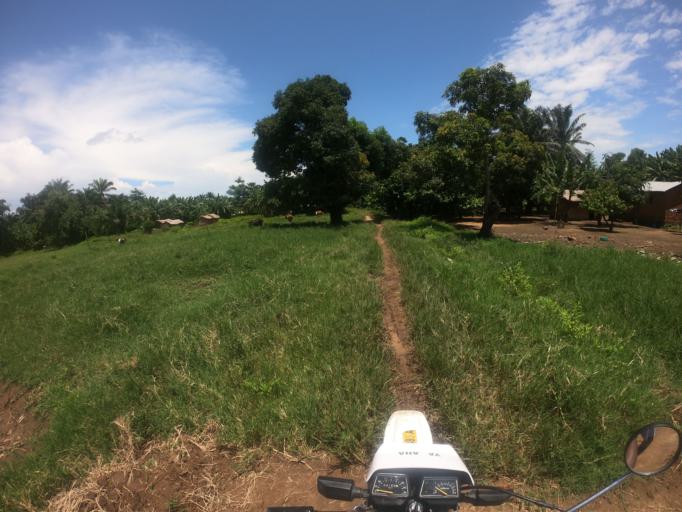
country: TZ
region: Mbeya
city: Kyela
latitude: -9.6562
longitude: 33.8228
